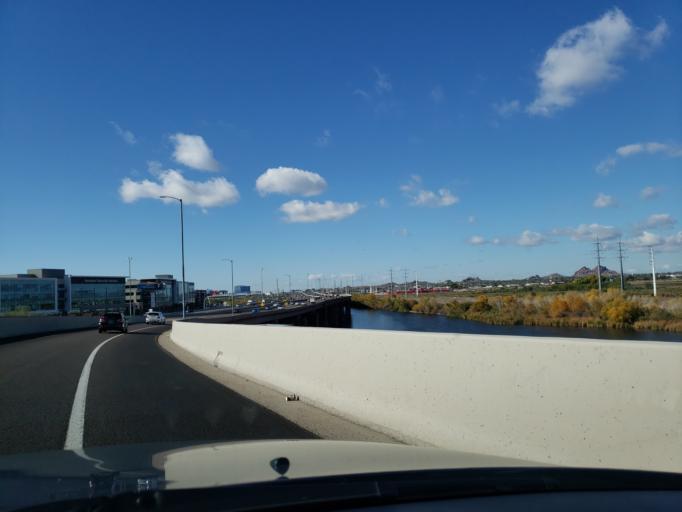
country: US
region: Arizona
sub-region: Maricopa County
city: Tempe
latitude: 33.4359
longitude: -111.8942
